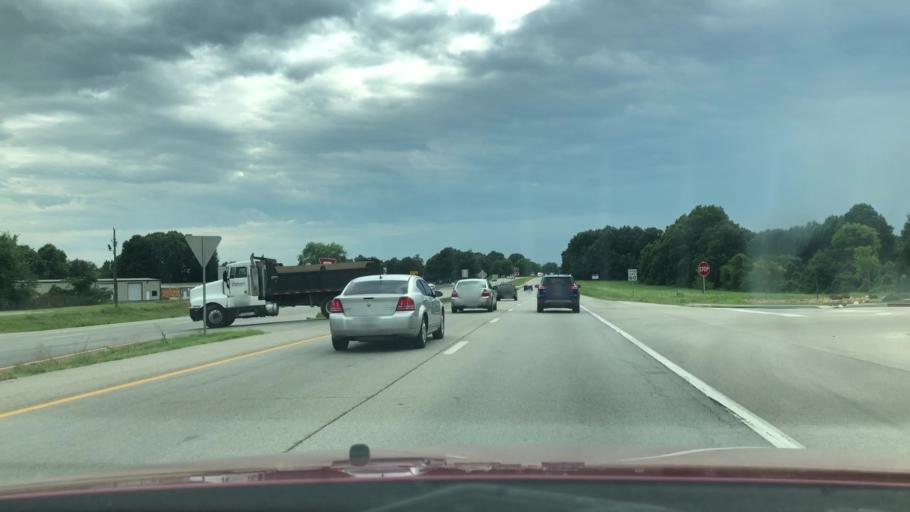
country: US
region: Missouri
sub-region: Greene County
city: Republic
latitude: 37.1454
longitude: -93.4301
